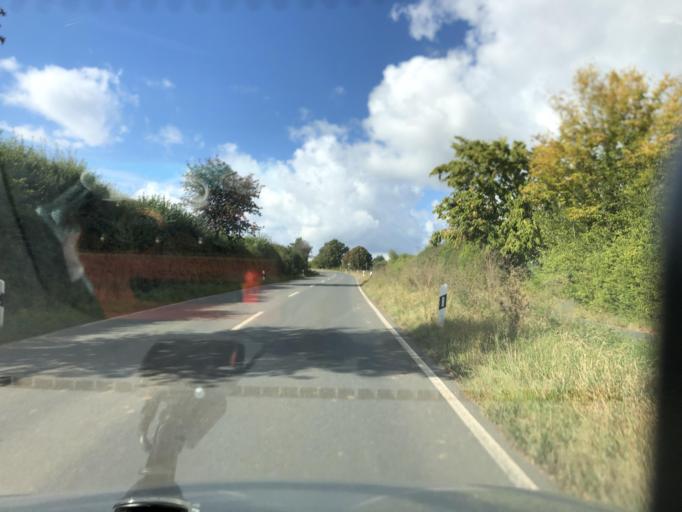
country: DE
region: Bavaria
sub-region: Regierungsbezirk Mittelfranken
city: Zirndorf
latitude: 49.4459
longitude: 10.9249
